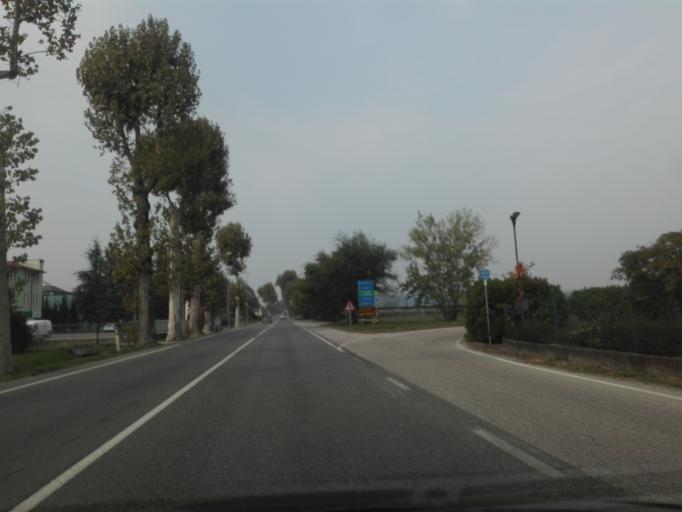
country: IT
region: Veneto
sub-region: Provincia di Verona
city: Sona
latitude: 45.4461
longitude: 10.8504
